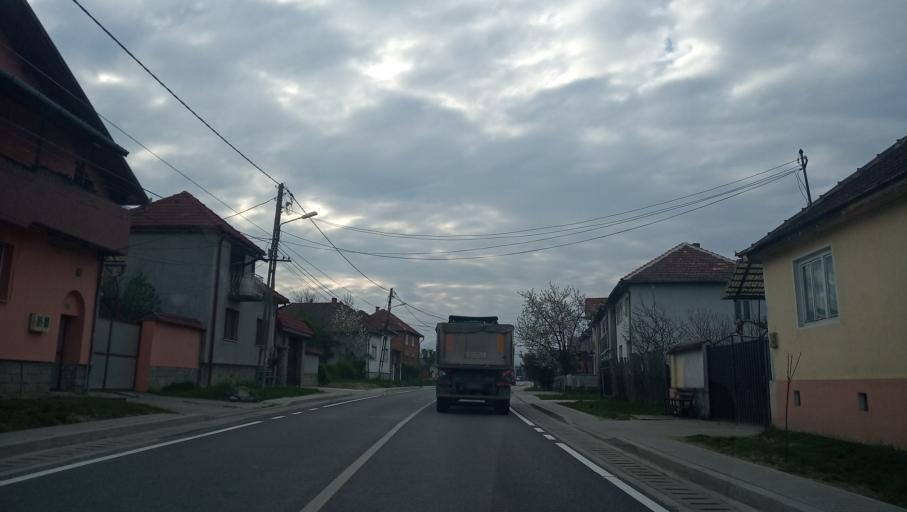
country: RO
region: Bihor
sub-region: Comuna Rieni
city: Ghighiseni
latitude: 46.5472
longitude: 22.4521
